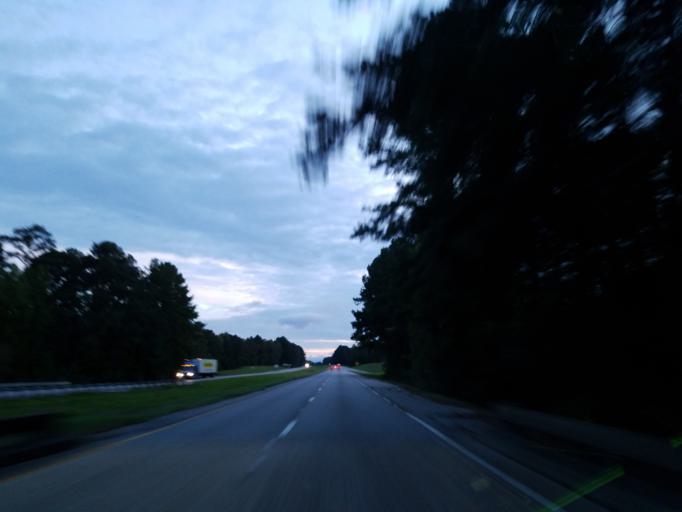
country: US
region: Mississippi
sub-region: Clarke County
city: Stonewall
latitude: 32.2040
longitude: -88.8447
